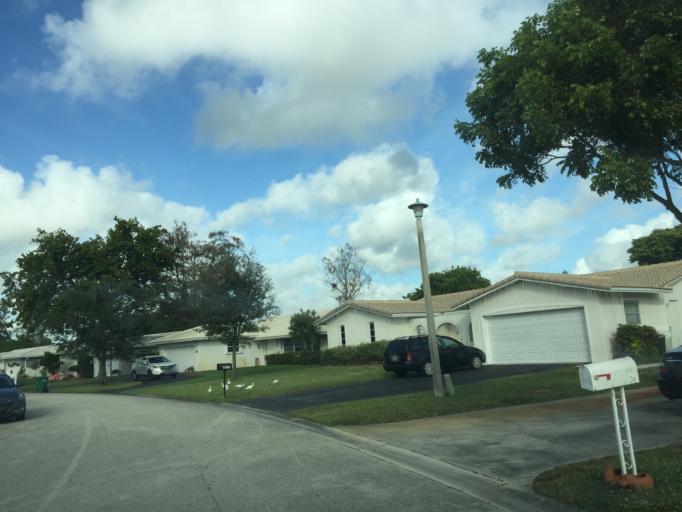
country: US
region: Florida
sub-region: Broward County
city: Margate
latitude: 26.2471
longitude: -80.2383
